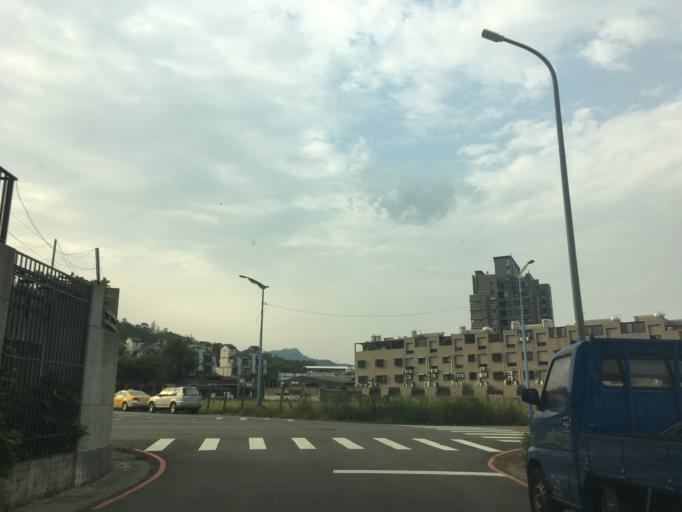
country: TW
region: Taiwan
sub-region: Taichung City
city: Taichung
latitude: 24.1719
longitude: 120.7327
